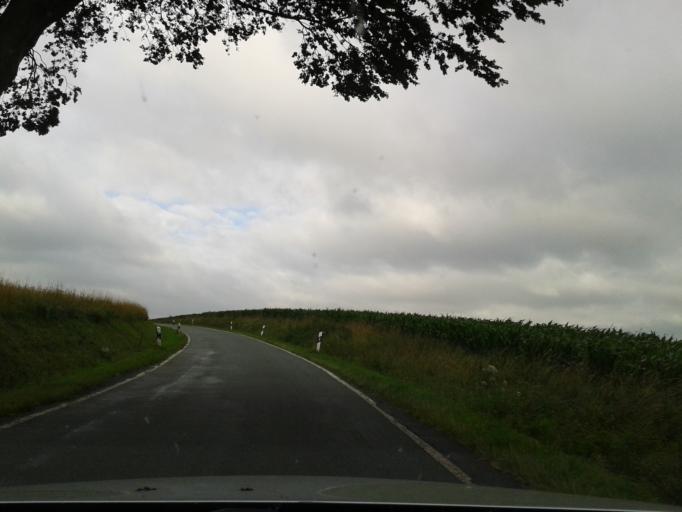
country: DE
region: North Rhine-Westphalia
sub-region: Regierungsbezirk Detmold
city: Dorentrup
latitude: 52.0108
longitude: 9.0108
